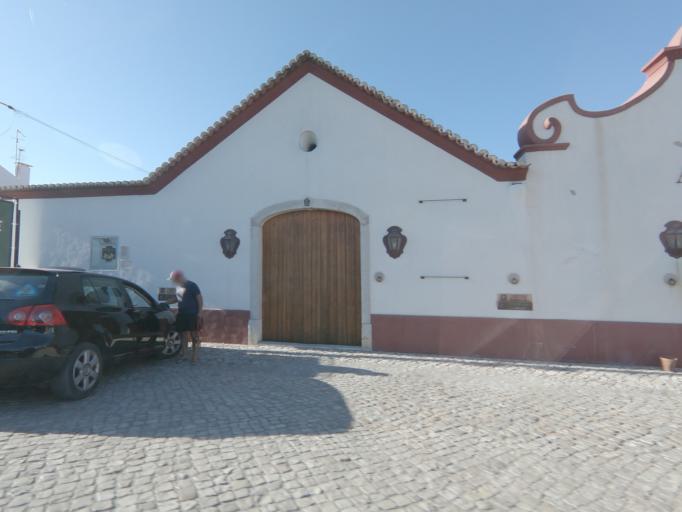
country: PT
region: Setubal
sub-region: Palmela
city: Quinta do Anjo
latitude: 38.5674
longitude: -8.9408
